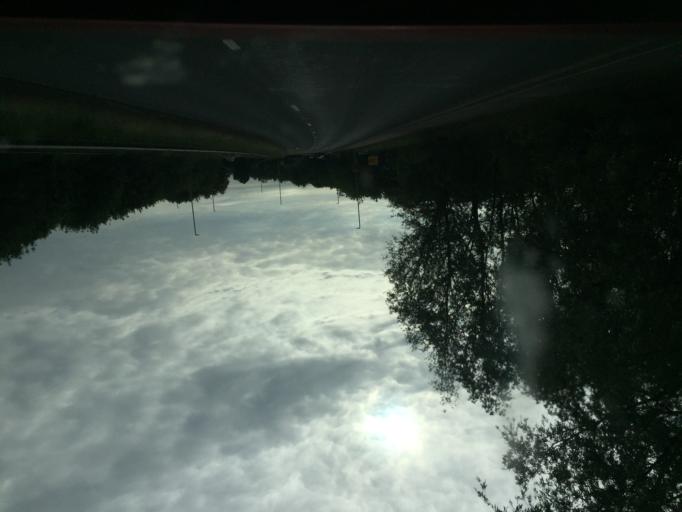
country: GB
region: England
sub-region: Leicestershire
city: Lutterworth
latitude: 52.4533
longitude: -1.2268
